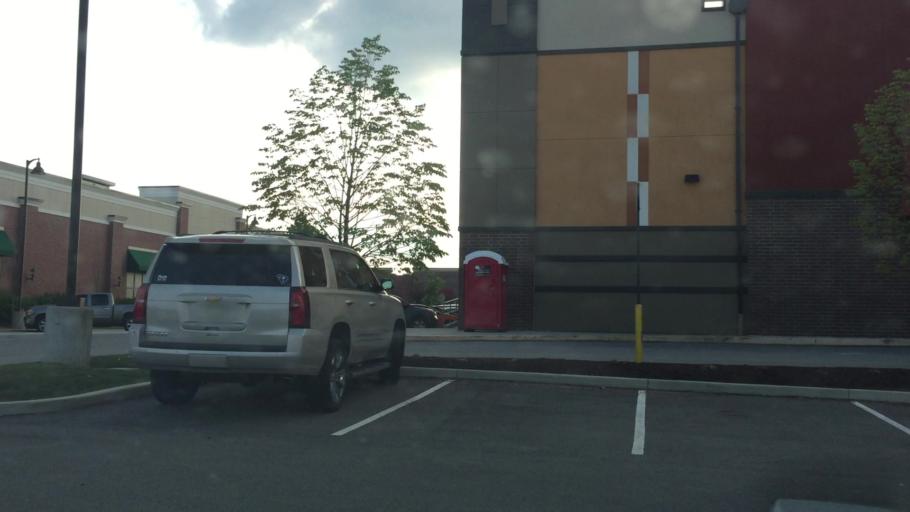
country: US
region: Pennsylvania
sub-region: Allegheny County
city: West View
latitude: 40.5701
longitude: -80.0191
